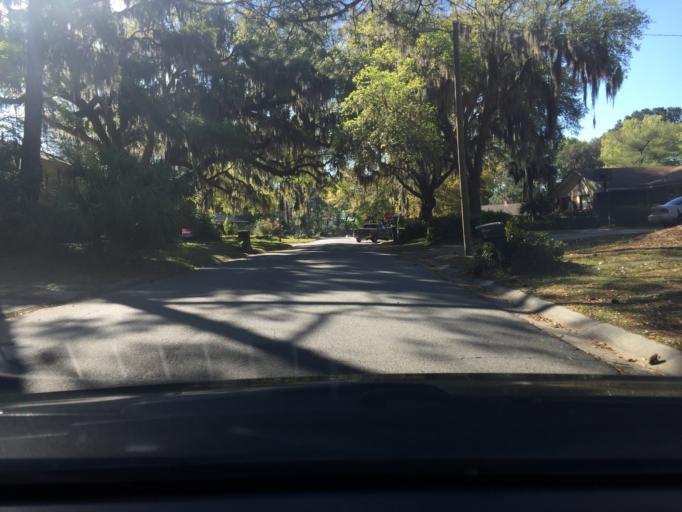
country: US
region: Georgia
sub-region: Chatham County
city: Montgomery
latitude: 31.9855
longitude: -81.1251
